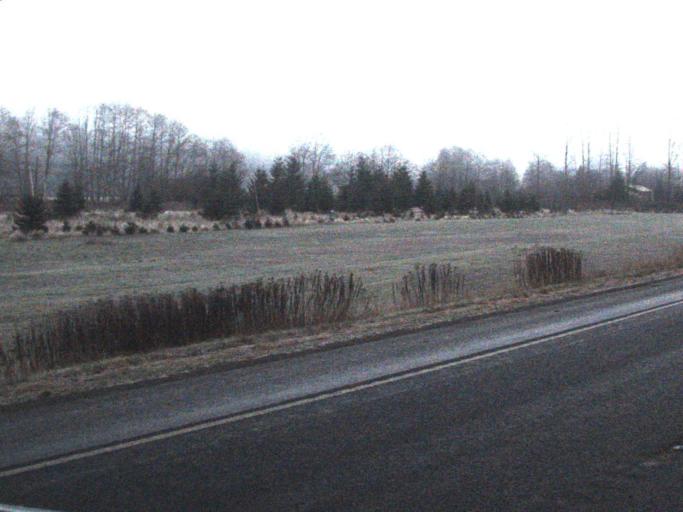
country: US
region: Washington
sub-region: Skagit County
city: Sedro-Woolley
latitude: 48.5229
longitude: -121.9609
